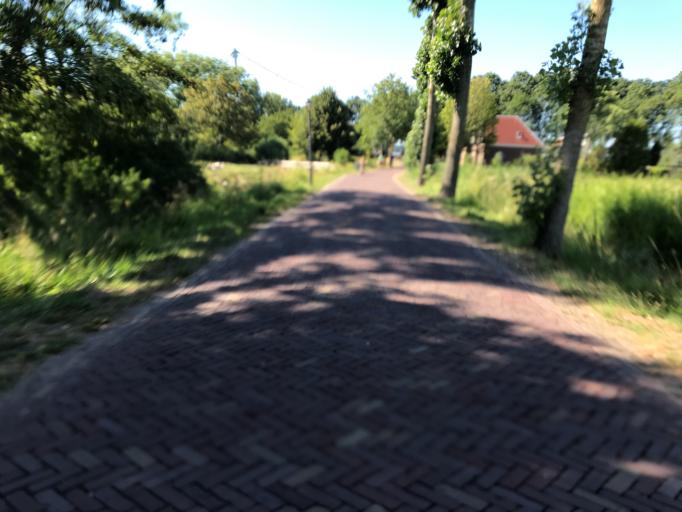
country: NL
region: North Holland
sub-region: Gemeente Diemen
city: Diemen
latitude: 52.3542
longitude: 4.9706
